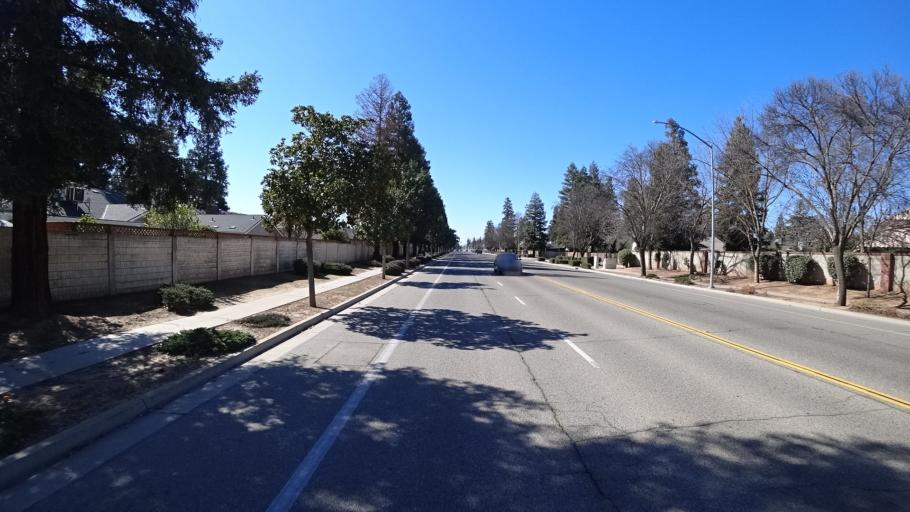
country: US
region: California
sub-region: Fresno County
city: Clovis
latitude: 36.8592
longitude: -119.7533
